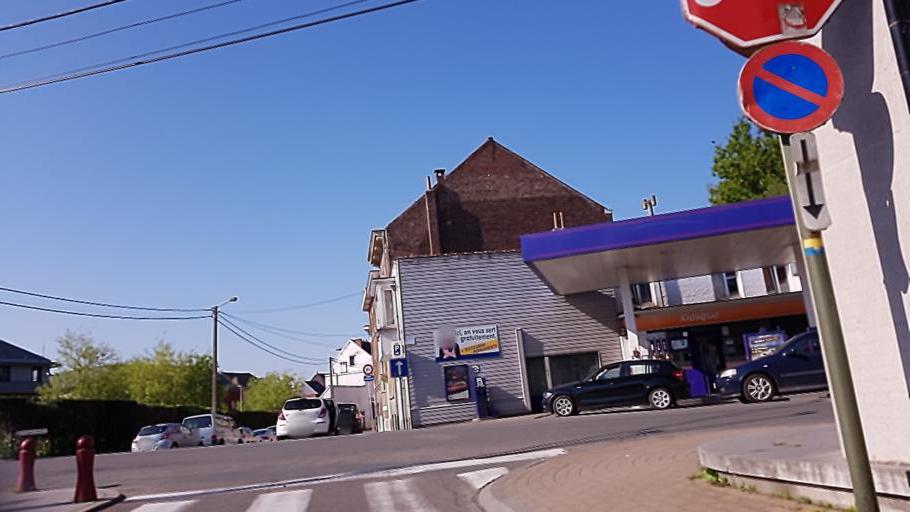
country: BE
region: Wallonia
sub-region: Province du Brabant Wallon
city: Wavre
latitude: 50.7177
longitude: 4.6150
